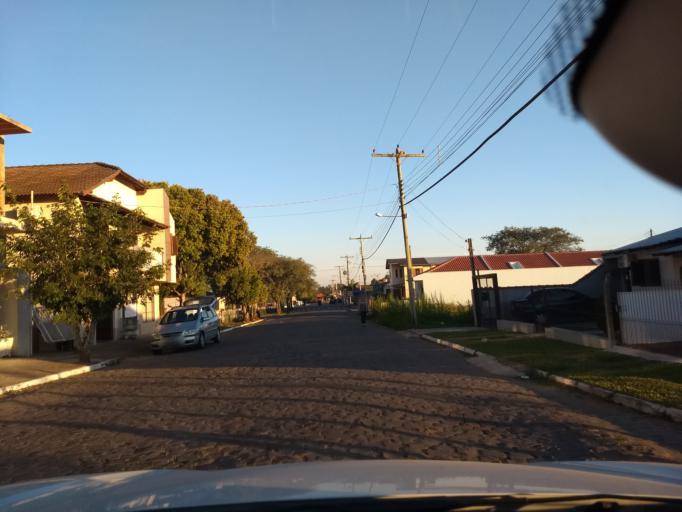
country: BR
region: Rio Grande do Sul
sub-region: Santa Cruz Do Sul
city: Santa Cruz do Sul
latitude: -29.7169
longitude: -52.5150
